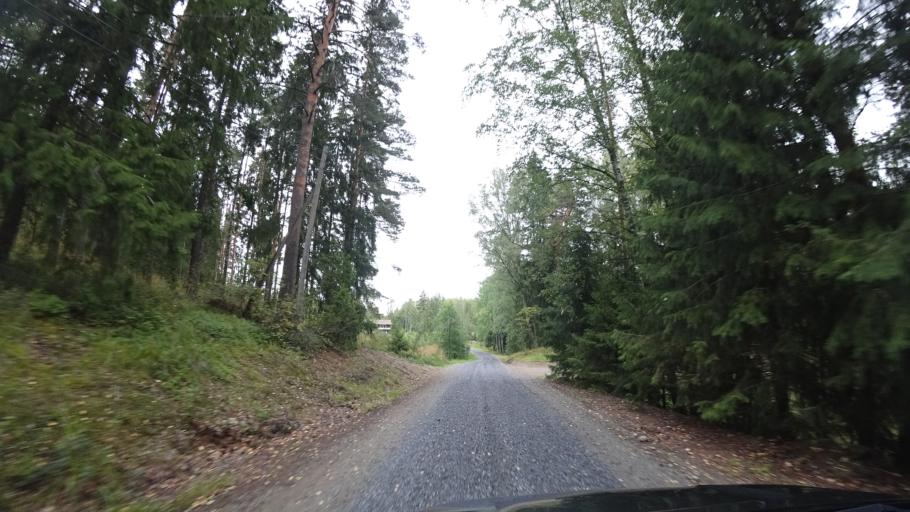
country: FI
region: Haeme
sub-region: Haemeenlinna
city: Lammi
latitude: 61.1228
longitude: 24.9838
